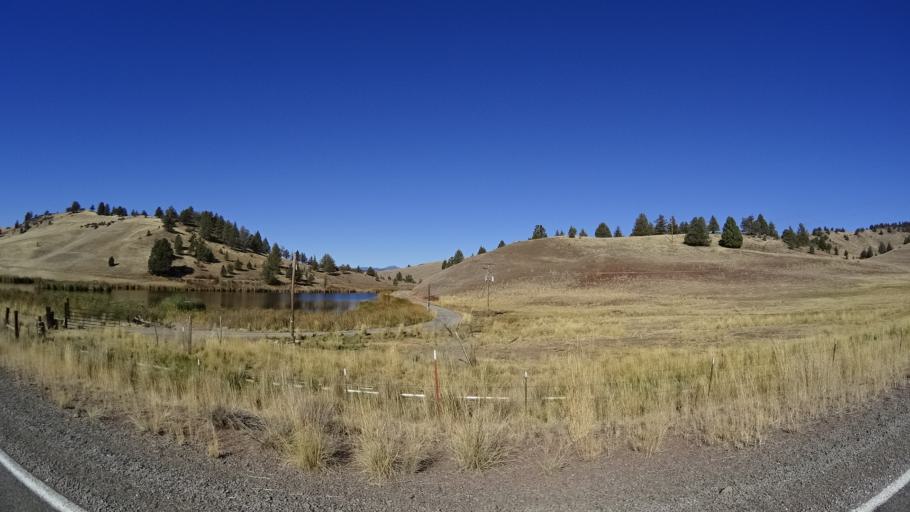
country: US
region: California
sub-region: Siskiyou County
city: Montague
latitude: 41.9209
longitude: -122.3722
